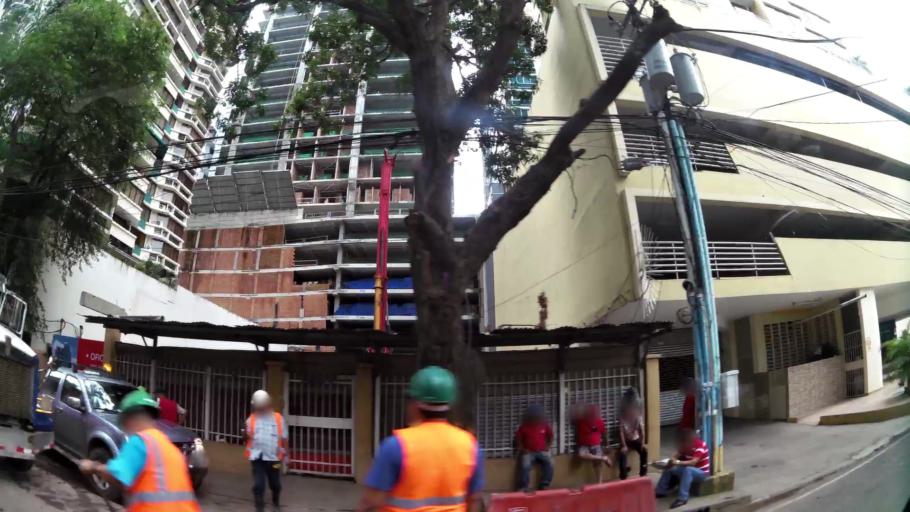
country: PA
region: Panama
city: Panama
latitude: 8.9767
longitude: -79.5247
